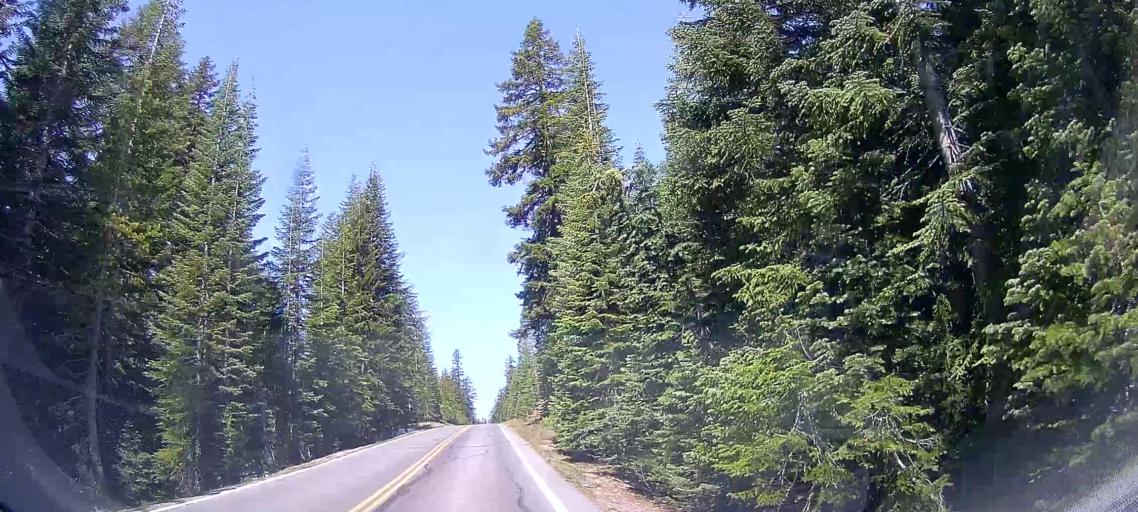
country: US
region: Oregon
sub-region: Klamath County
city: Klamath Falls
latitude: 42.8796
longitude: -122.1133
